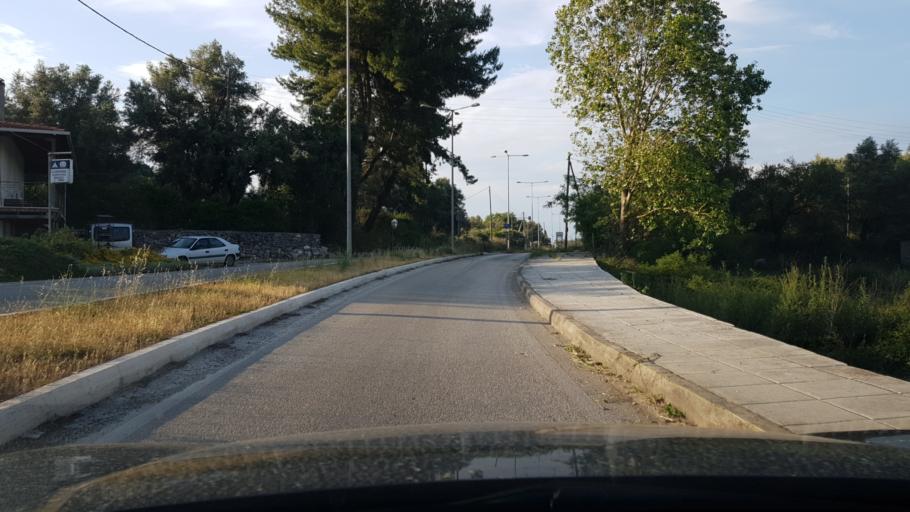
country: GR
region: Ionian Islands
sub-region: Lefkada
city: Lefkada
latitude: 38.8046
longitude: 20.7148
